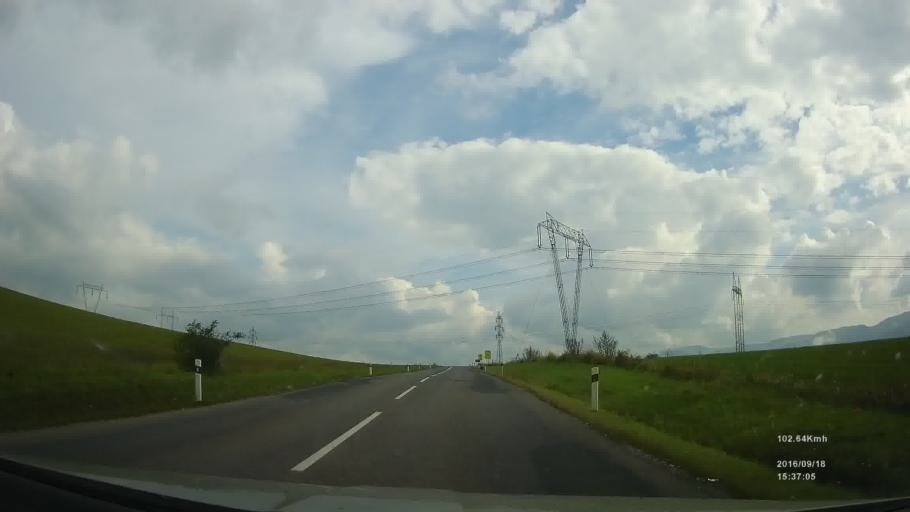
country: SK
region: Kosicky
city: Spisska Nova Ves
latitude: 48.9879
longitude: 20.4767
